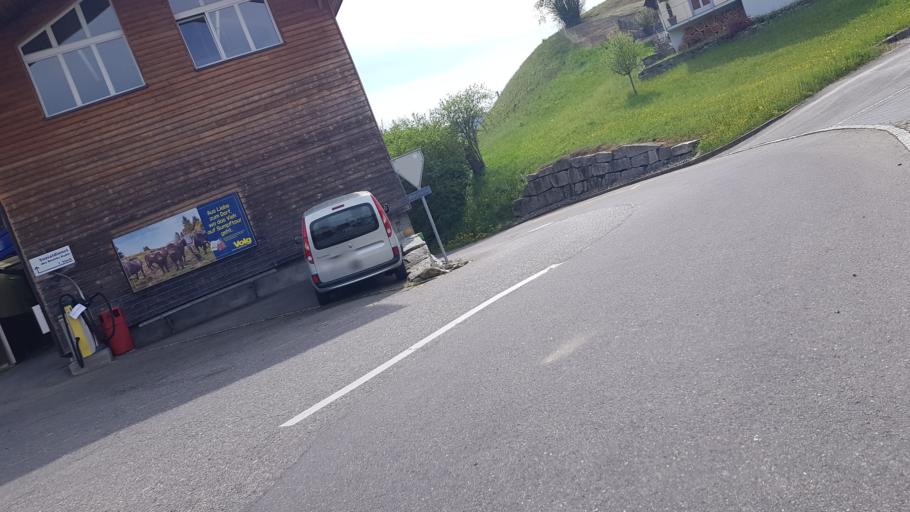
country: CH
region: Aargau
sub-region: Bezirk Kulm
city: Gontenschwil
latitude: 47.2836
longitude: 8.1531
